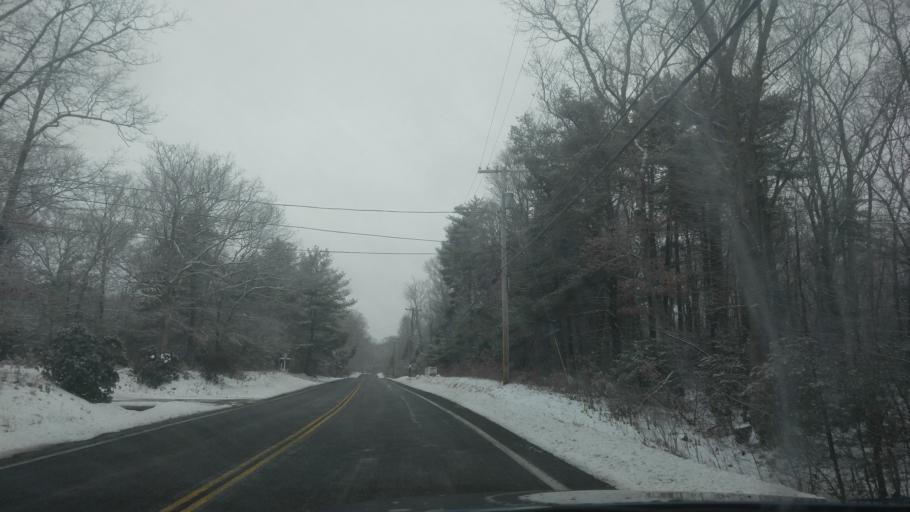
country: US
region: Rhode Island
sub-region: Providence County
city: Foster
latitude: 41.8167
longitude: -71.7358
